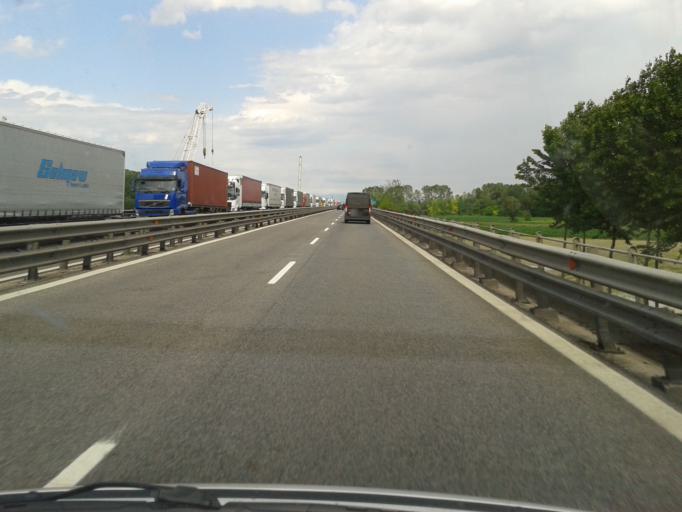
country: IT
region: Friuli Venezia Giulia
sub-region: Provincia di Udine
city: Ronchis
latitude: 45.8131
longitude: 12.9855
